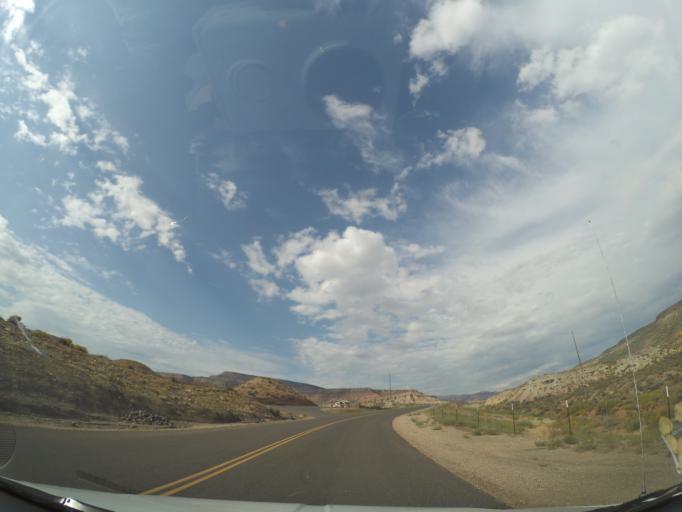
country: US
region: Utah
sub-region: Washington County
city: LaVerkin
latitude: 37.2062
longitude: -113.1752
